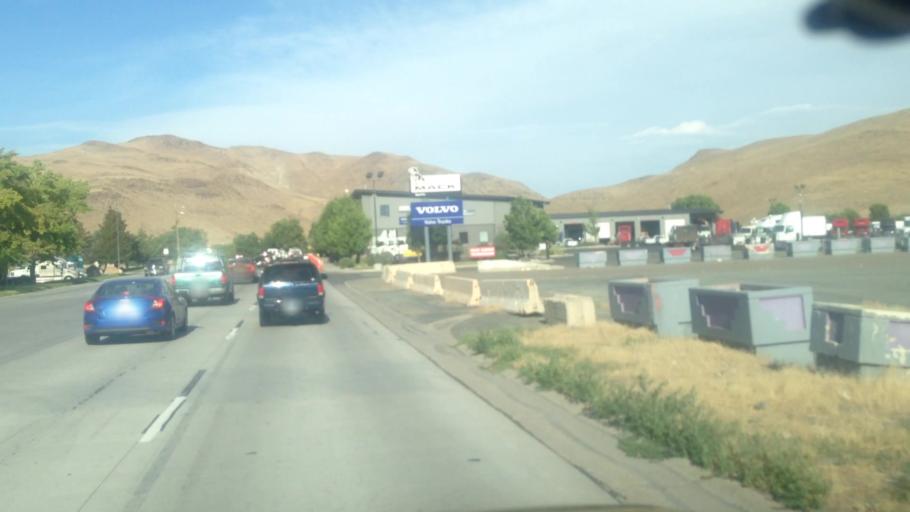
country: US
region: Nevada
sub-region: Washoe County
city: Sparks
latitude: 39.5225
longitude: -119.7084
